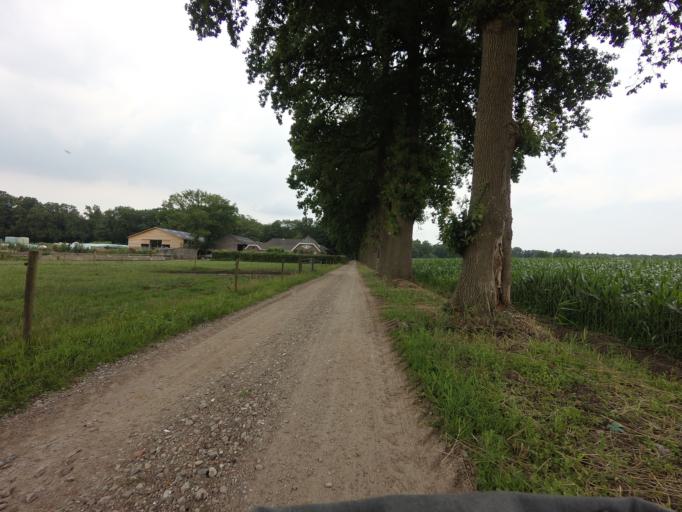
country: NL
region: Utrecht
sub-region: Gemeente Utrechtse Heuvelrug
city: Doorn
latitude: 52.0274
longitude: 5.3258
